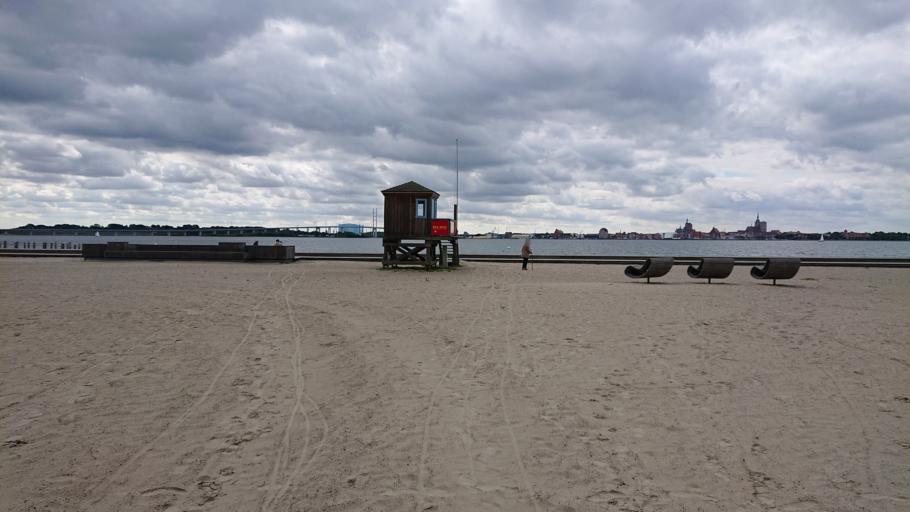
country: DE
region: Mecklenburg-Vorpommern
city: Altefahr
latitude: 54.3308
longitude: 13.1197
